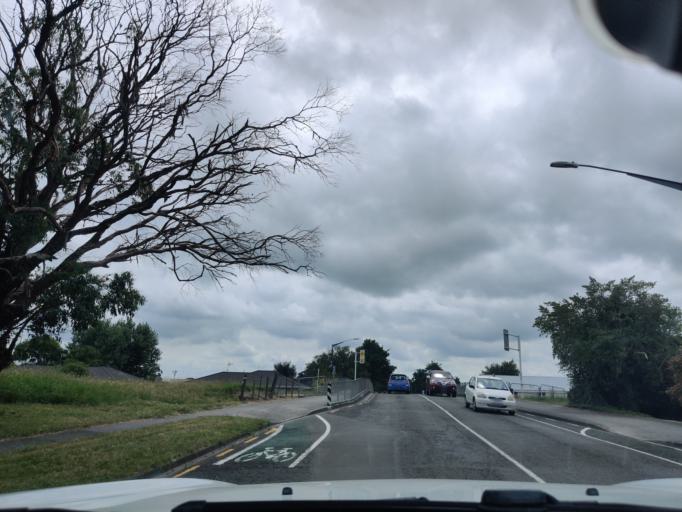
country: NZ
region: Manawatu-Wanganui
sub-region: Palmerston North City
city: Palmerston North
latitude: -40.3537
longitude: 175.5869
